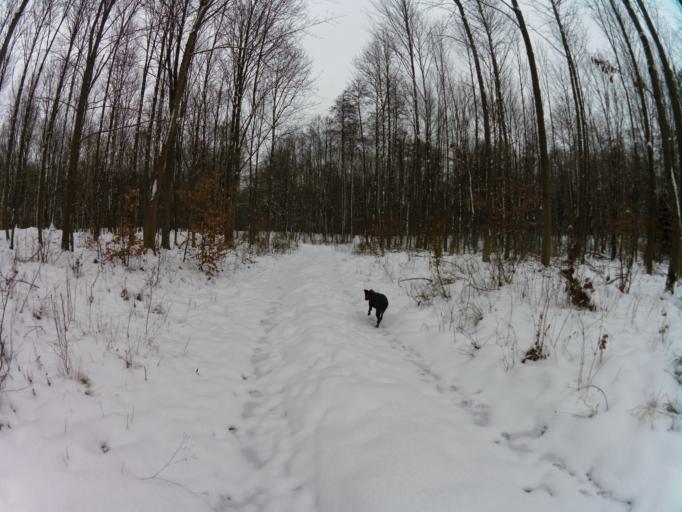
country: PL
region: West Pomeranian Voivodeship
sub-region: Powiat choszczenski
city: Recz
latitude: 53.3287
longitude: 15.5451
